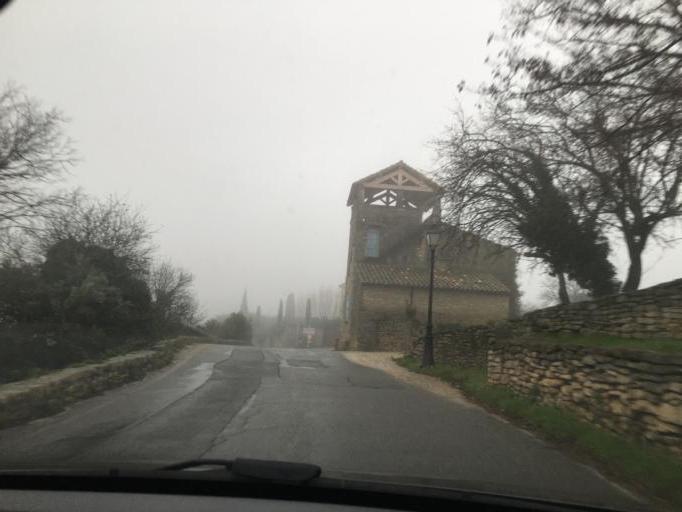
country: FR
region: Provence-Alpes-Cote d'Azur
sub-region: Departement du Vaucluse
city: Gordes
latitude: 43.9124
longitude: 5.1965
